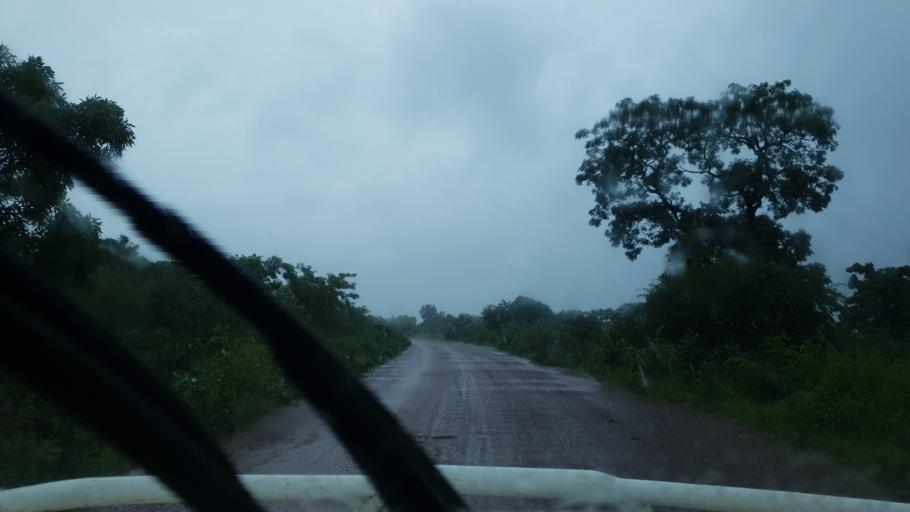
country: ML
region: Sikasso
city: Kolondieba
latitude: 11.6071
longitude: -6.6752
